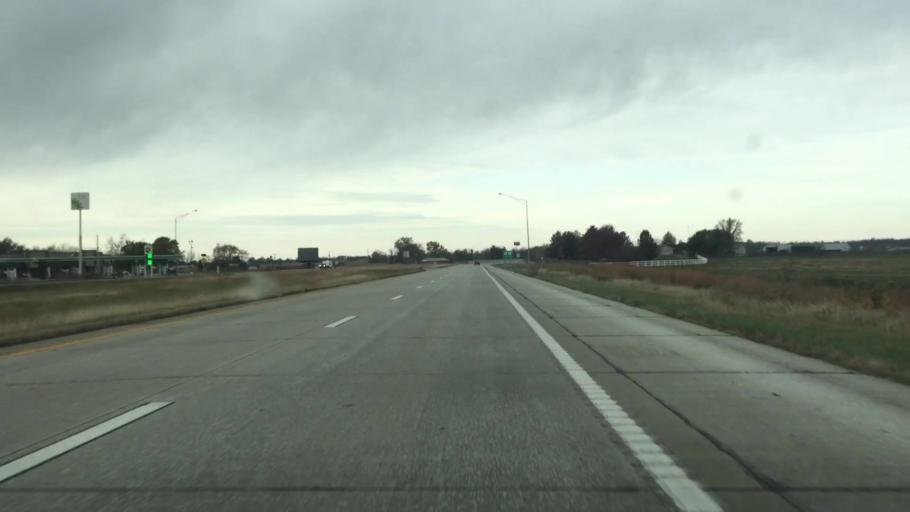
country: US
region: Missouri
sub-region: Saint Clair County
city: Osceola
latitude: 38.1412
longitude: -93.7189
